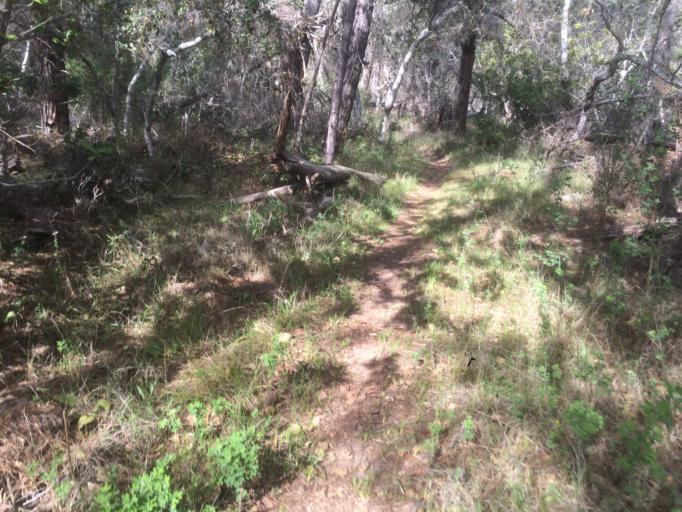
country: US
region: California
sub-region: San Luis Obispo County
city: Cambria
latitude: 35.5696
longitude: -121.0904
